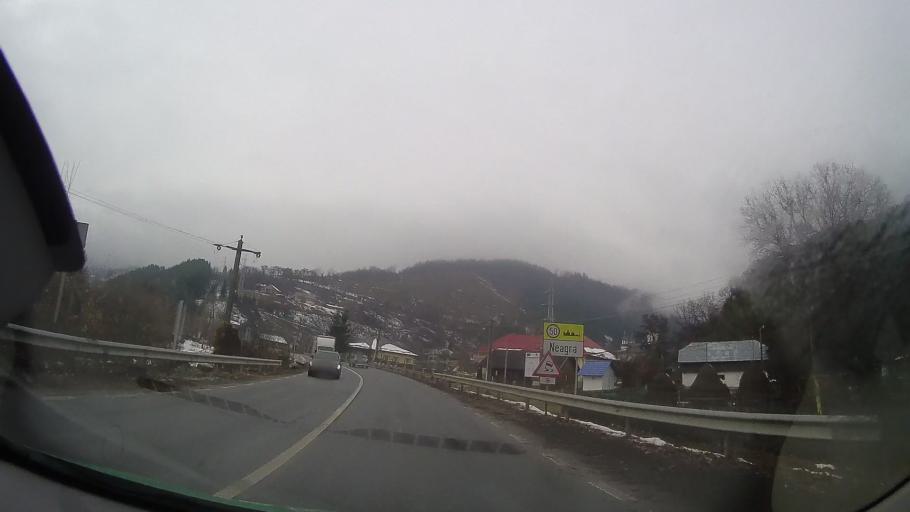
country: RO
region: Neamt
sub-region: Comuna Tasca
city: Tasca
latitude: 46.8794
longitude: 25.9838
